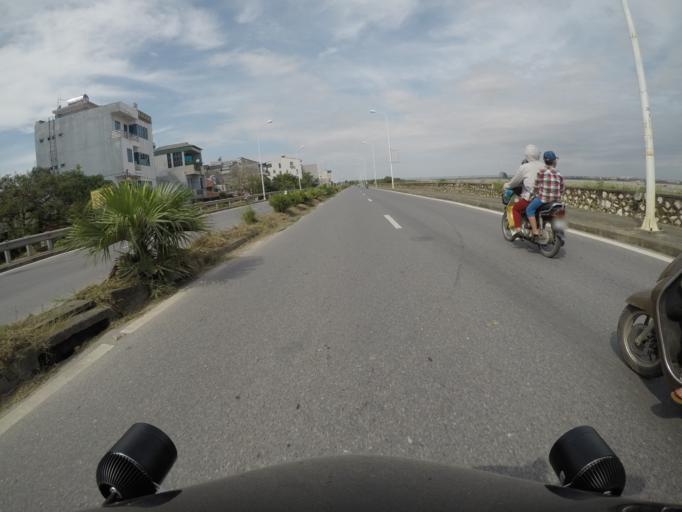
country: VN
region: Ha Noi
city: Tay Ho
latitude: 21.0898
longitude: 105.8077
